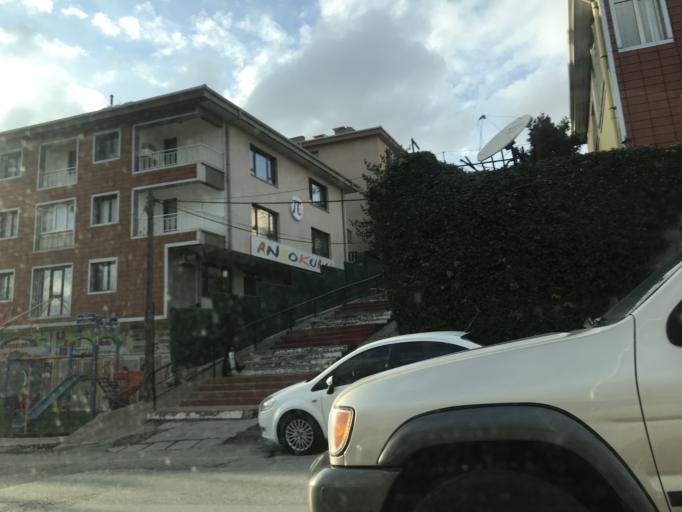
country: TR
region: Ankara
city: Mamak
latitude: 39.9692
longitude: 32.8757
